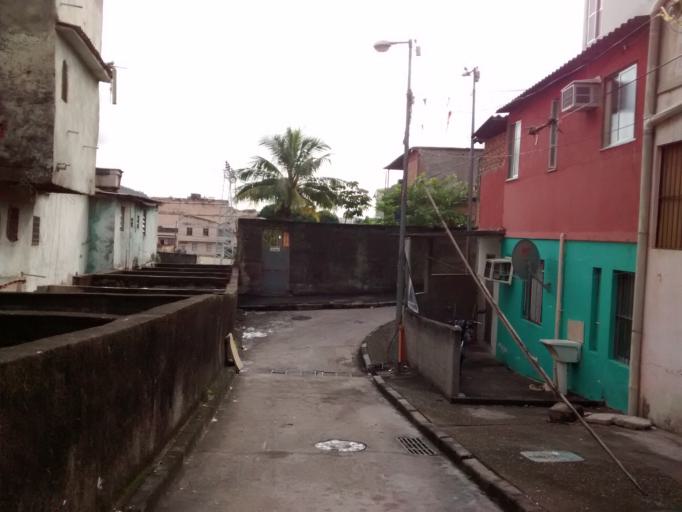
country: BR
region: Rio de Janeiro
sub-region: Rio De Janeiro
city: Rio de Janeiro
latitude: -22.9318
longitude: -43.2561
